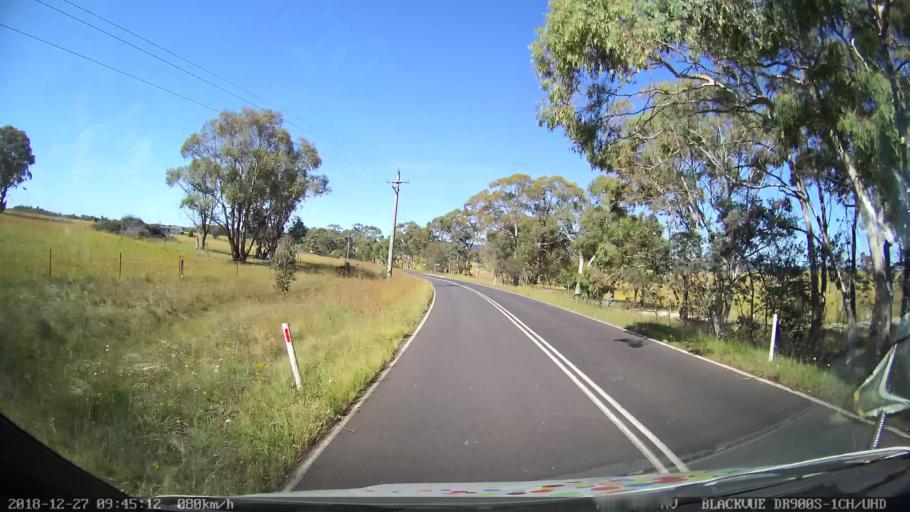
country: AU
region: New South Wales
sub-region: Lithgow
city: Portland
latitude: -33.3220
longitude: 149.9860
